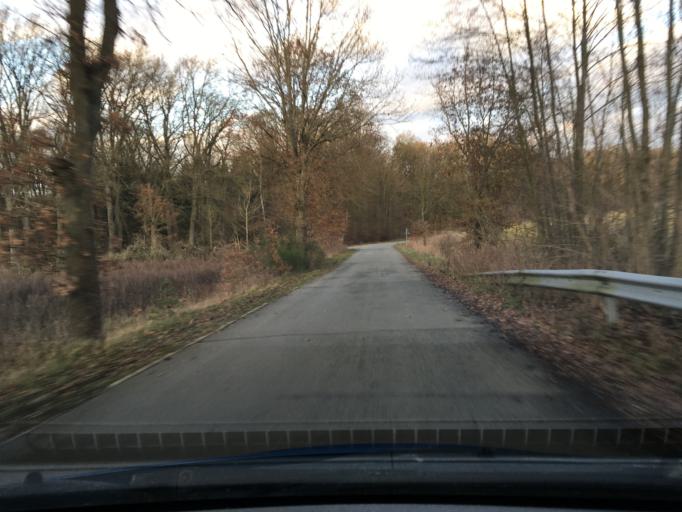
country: DE
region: Lower Saxony
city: Amelinghausen
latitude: 53.1393
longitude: 10.1893
